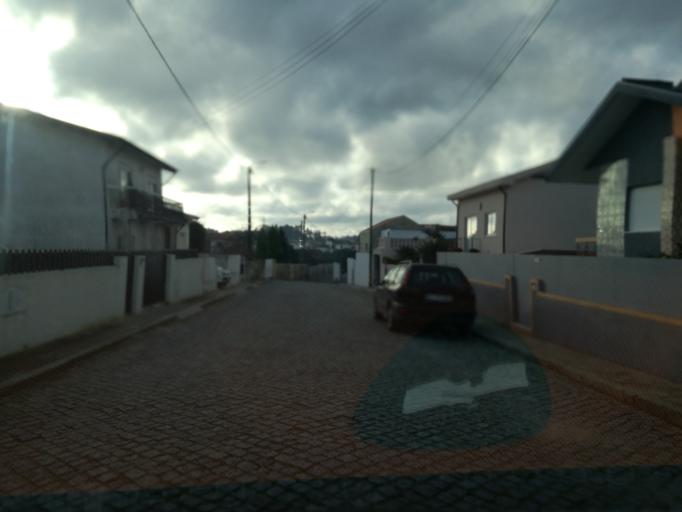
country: PT
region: Porto
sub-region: Maia
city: Nogueira
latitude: 41.2558
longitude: -8.5987
